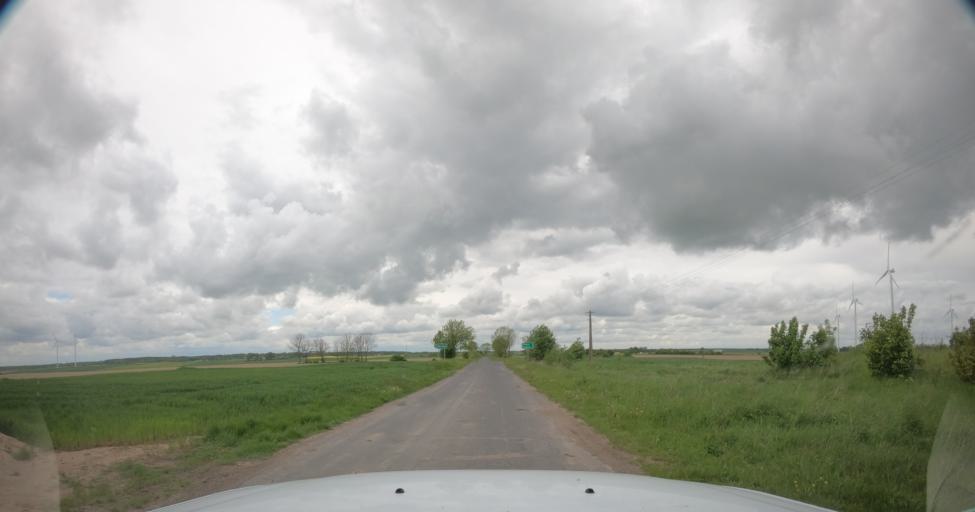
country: PL
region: West Pomeranian Voivodeship
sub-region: Powiat pyrzycki
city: Kozielice
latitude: 53.0956
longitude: 14.8033
